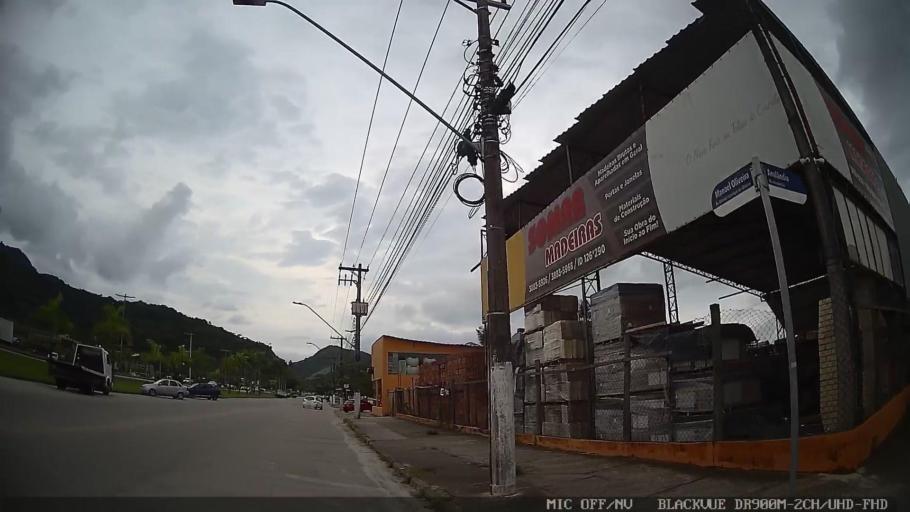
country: BR
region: Sao Paulo
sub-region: Caraguatatuba
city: Caraguatatuba
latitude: -23.6162
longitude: -45.3903
